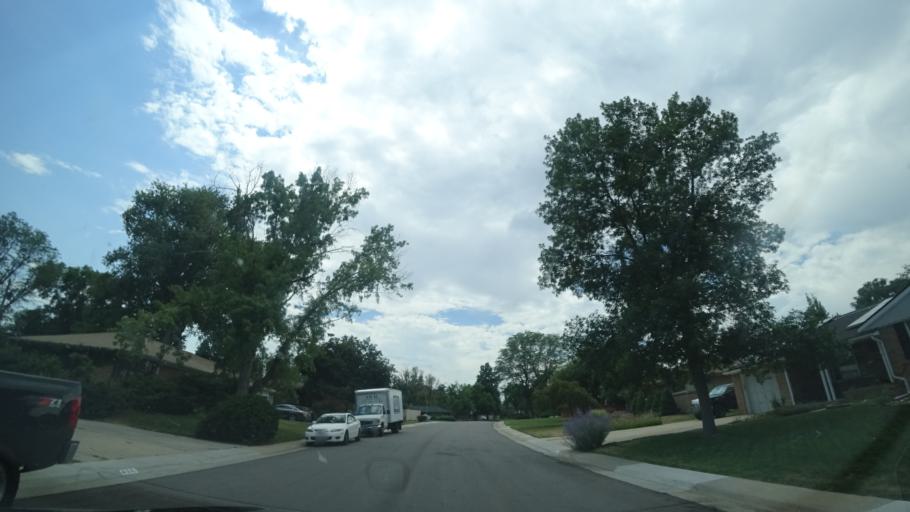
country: US
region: Colorado
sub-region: Jefferson County
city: Lakewood
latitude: 39.7234
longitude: -105.0945
